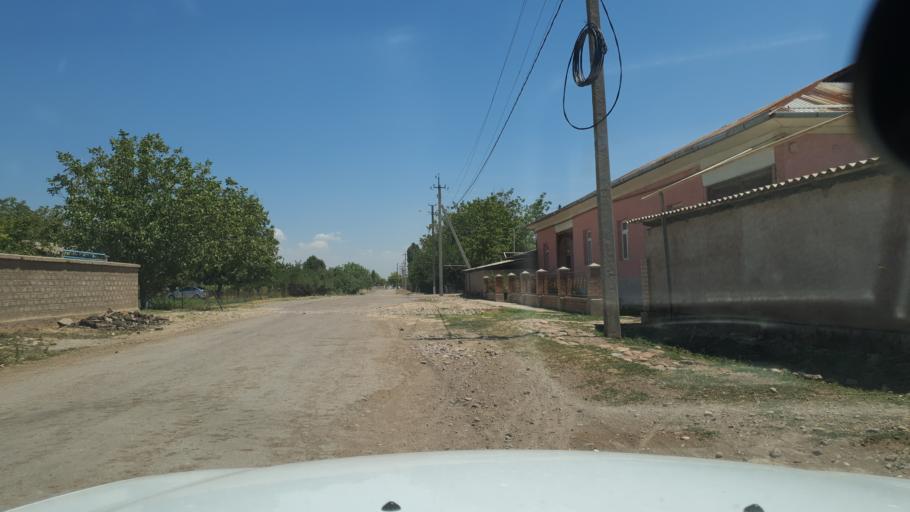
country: UZ
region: Toshkent
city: Piskent
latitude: 40.8256
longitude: 69.4003
